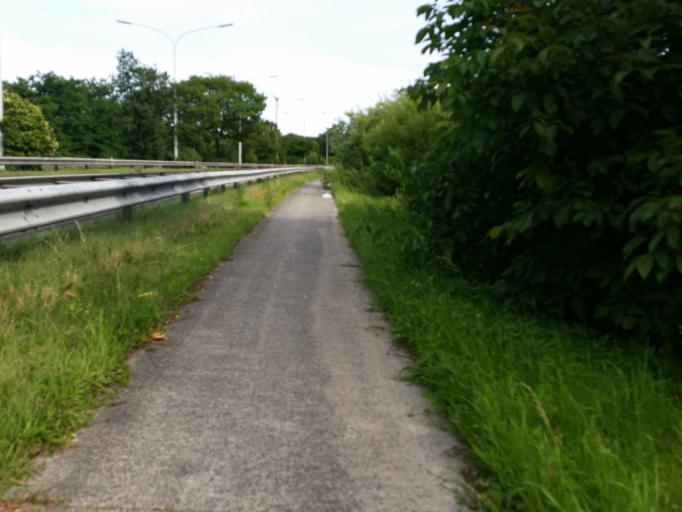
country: BE
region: Flanders
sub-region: Provincie Antwerpen
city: Puurs
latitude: 51.0764
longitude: 4.3005
